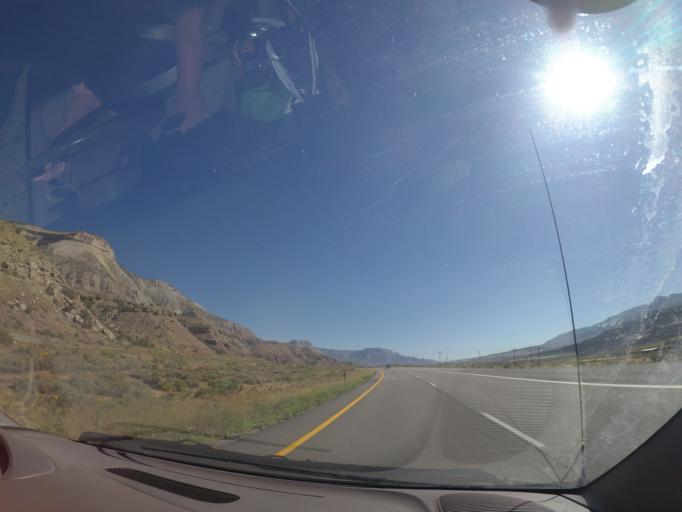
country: US
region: Colorado
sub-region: Garfield County
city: Parachute
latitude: 39.4108
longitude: -108.0961
